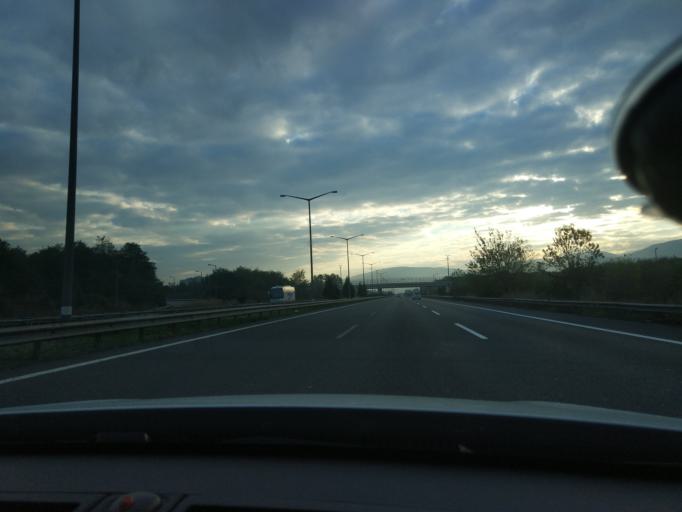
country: TR
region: Sakarya
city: Hendek
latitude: 40.7535
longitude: 30.7142
